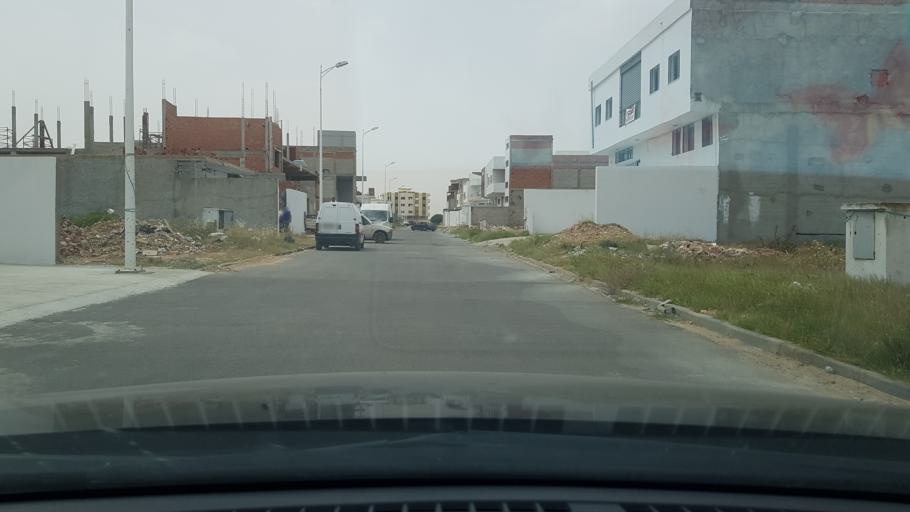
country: TN
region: Safaqis
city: Al Qarmadah
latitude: 34.8256
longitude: 10.7416
